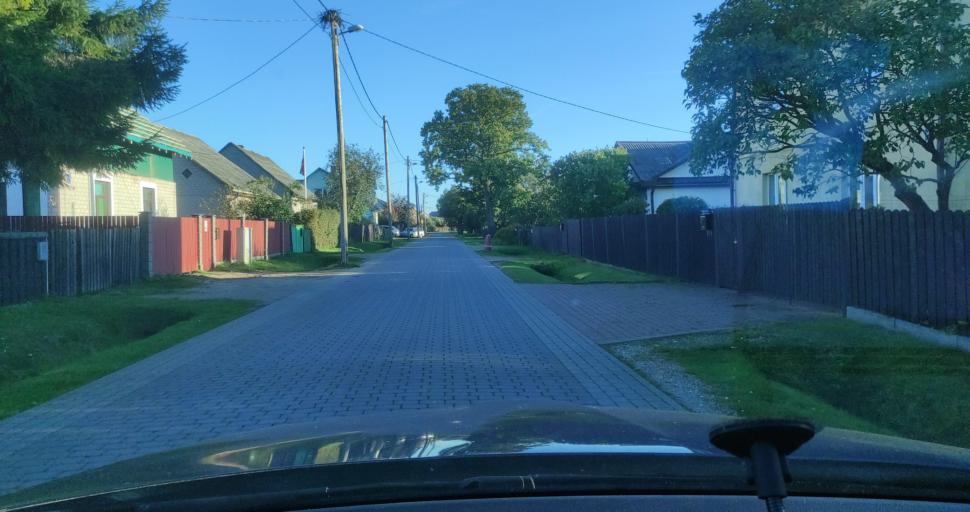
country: LV
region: Ventspils
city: Ventspils
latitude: 57.3755
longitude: 21.5765
